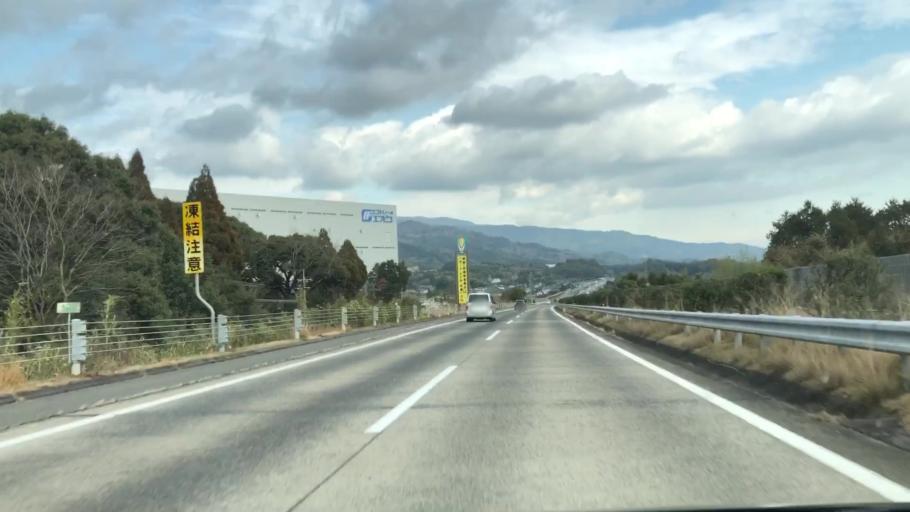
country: JP
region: Saga Prefecture
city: Kanzakimachi-kanzaki
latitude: 33.3432
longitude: 130.3597
